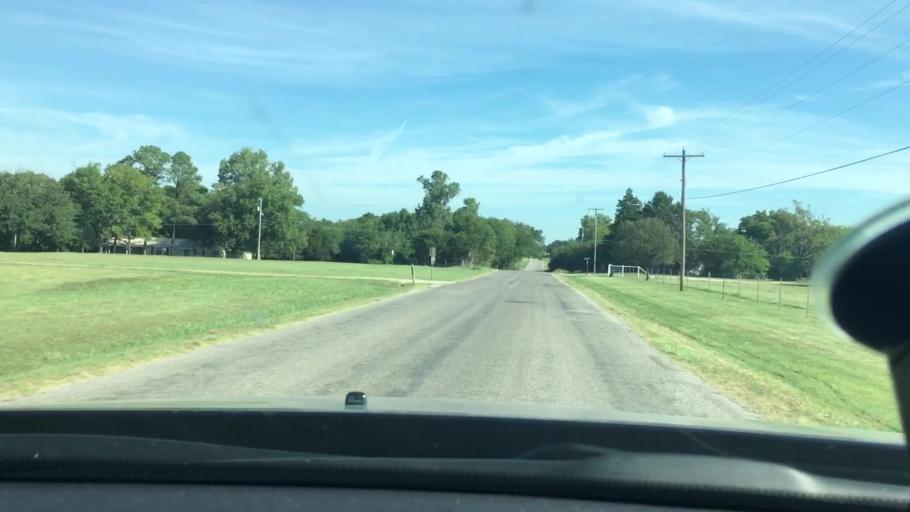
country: US
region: Oklahoma
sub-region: Carter County
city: Lone Grove
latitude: 34.2298
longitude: -97.2474
